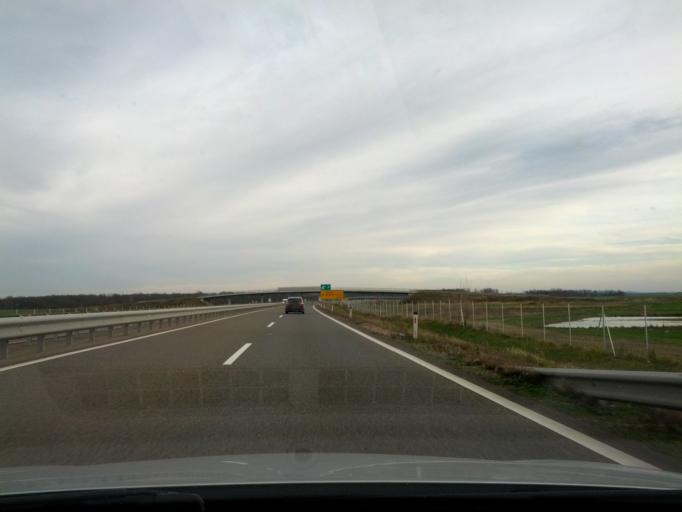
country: SI
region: Beltinci
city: Gancani
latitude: 46.6402
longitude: 16.2458
